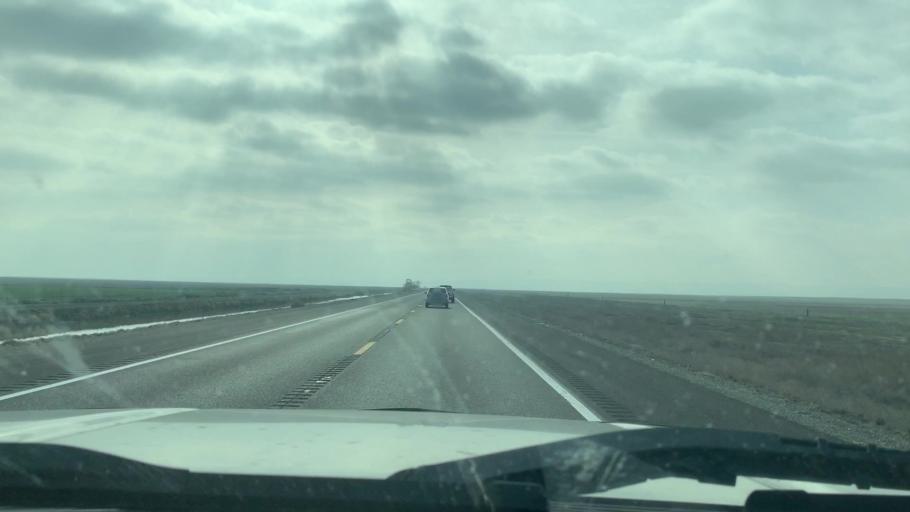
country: US
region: California
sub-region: Kings County
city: Stratford
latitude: 36.1124
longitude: -119.8992
